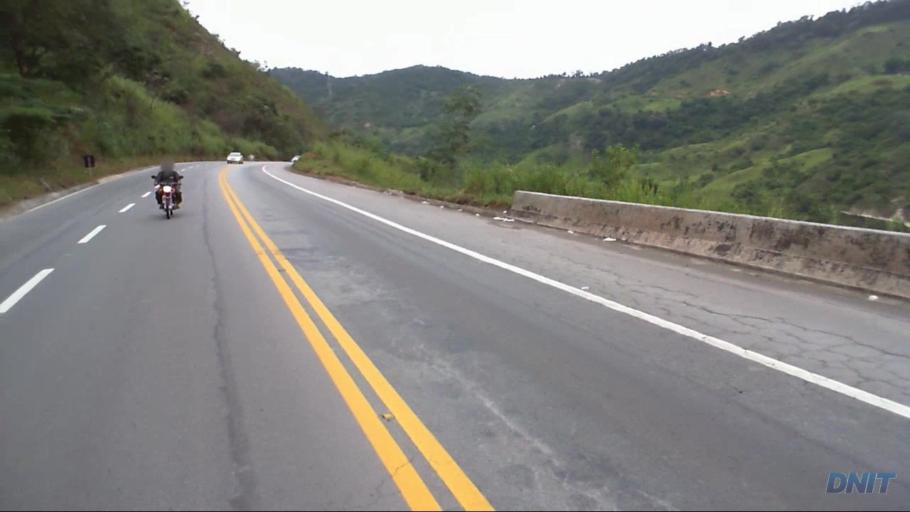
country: BR
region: Minas Gerais
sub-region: Timoteo
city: Timoteo
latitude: -19.6396
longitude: -42.8163
